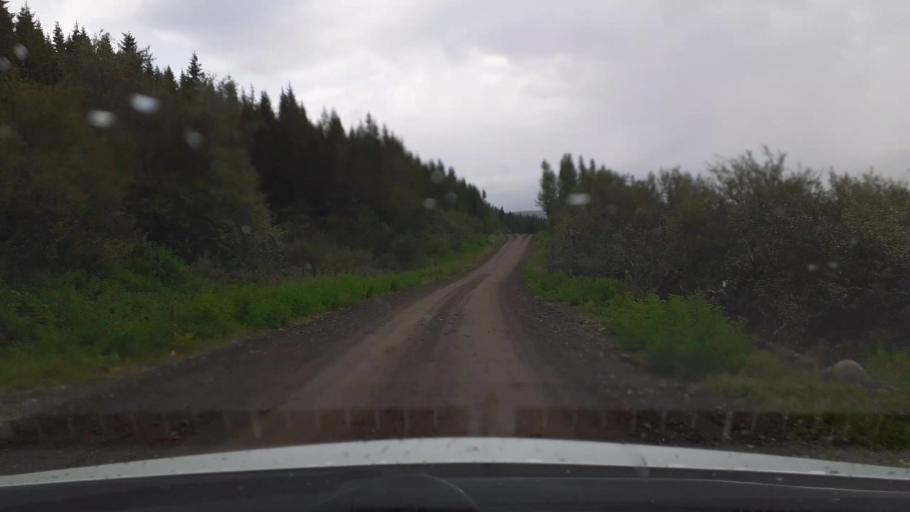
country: IS
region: Capital Region
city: Mosfellsbaer
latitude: 64.5175
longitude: -21.4221
